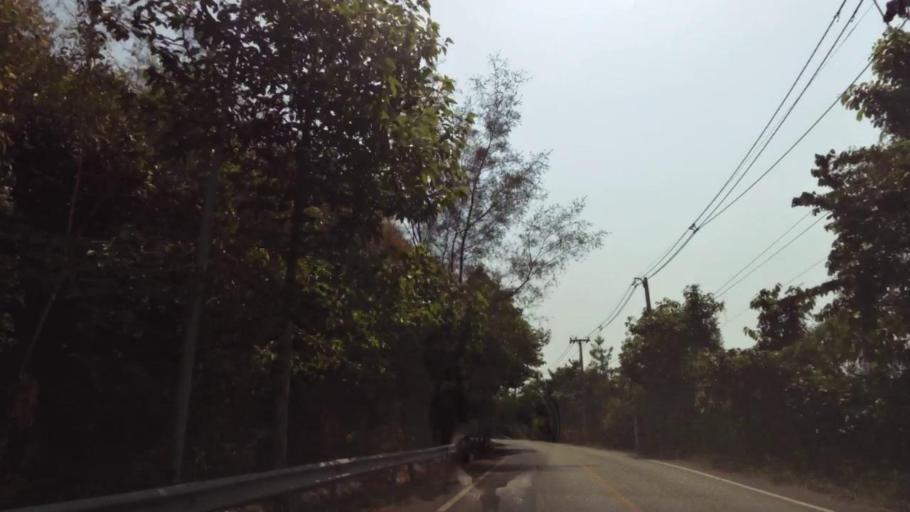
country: TH
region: Chanthaburi
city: Tha Mai
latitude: 12.5311
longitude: 101.9454
